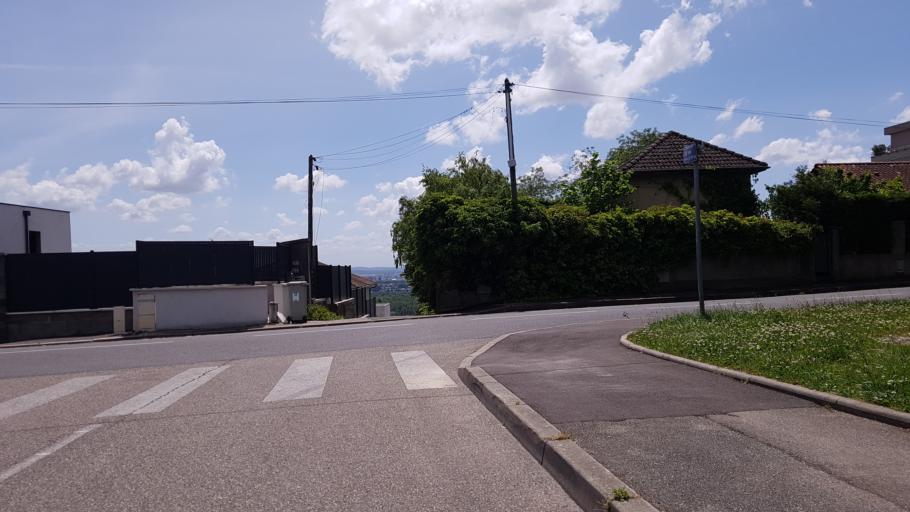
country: FR
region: Rhone-Alpes
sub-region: Departement du Rhone
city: Rillieux-la-Pape
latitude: 45.8102
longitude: 4.8910
